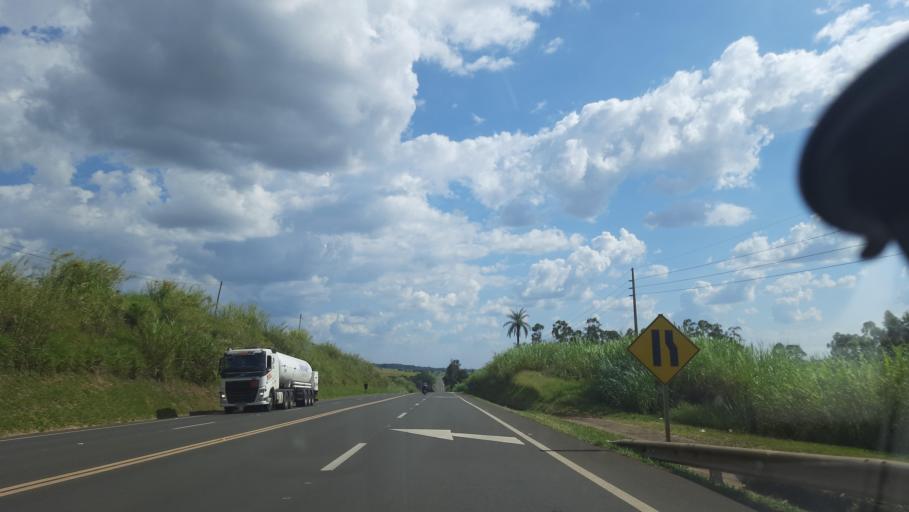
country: BR
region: Sao Paulo
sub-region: Sao Jose Do Rio Pardo
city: Sao Jose do Rio Pardo
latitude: -21.6607
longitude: -46.9174
